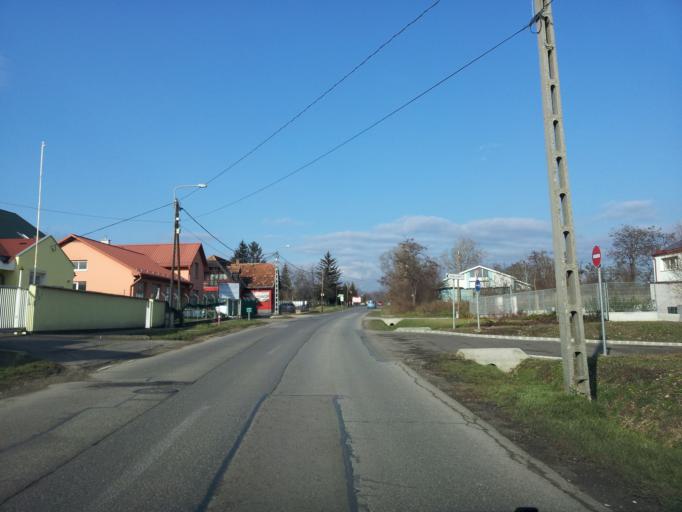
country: HU
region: Pest
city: Pomaz
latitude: 47.6333
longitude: 19.0403
